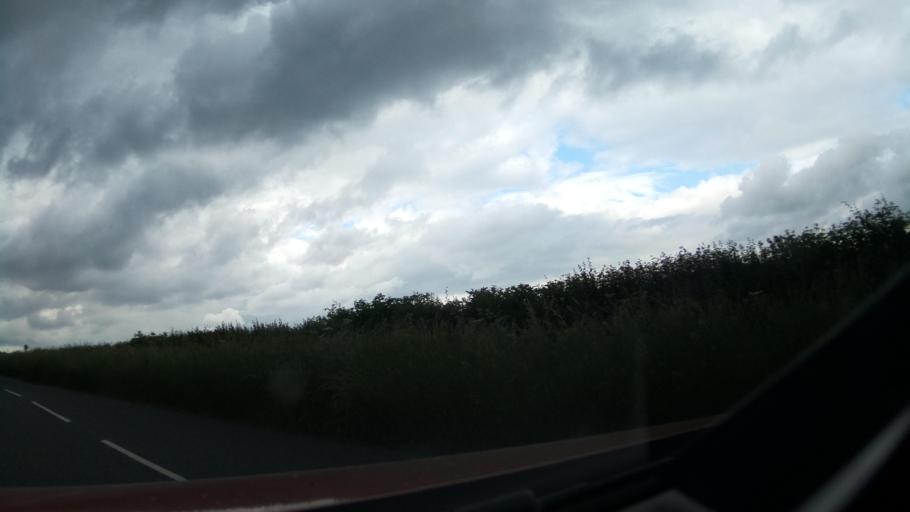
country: GB
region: England
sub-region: South Gloucestershire
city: Pucklechurch
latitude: 51.4781
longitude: -2.4275
